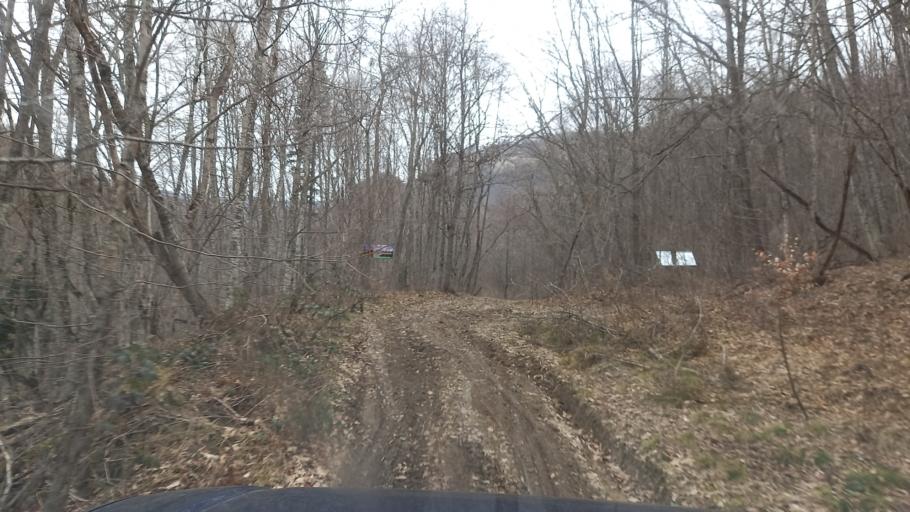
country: RU
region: Adygeya
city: Kamennomostskiy
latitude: 44.1110
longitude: 40.1040
